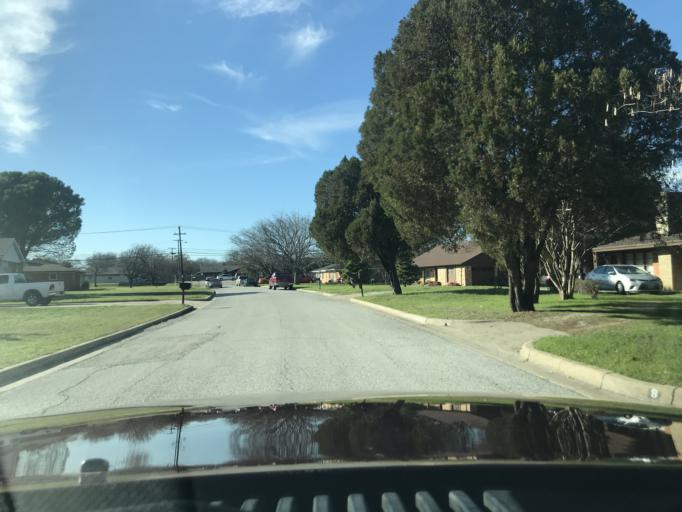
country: US
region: Texas
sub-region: Tarrant County
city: Edgecliff Village
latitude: 32.6572
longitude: -97.3471
